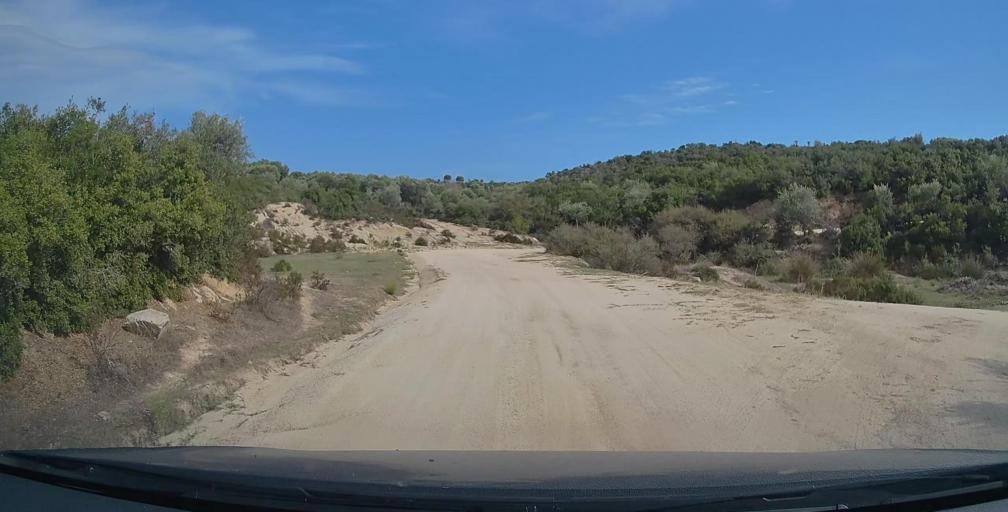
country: GR
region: Central Macedonia
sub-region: Nomos Chalkidikis
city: Sykia
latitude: 40.0046
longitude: 23.9241
